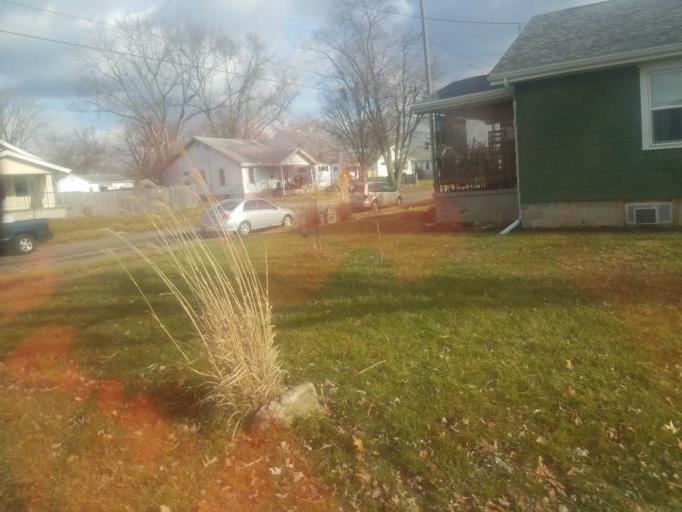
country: US
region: Ohio
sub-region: Marion County
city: Marion
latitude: 40.5762
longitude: -83.1504
